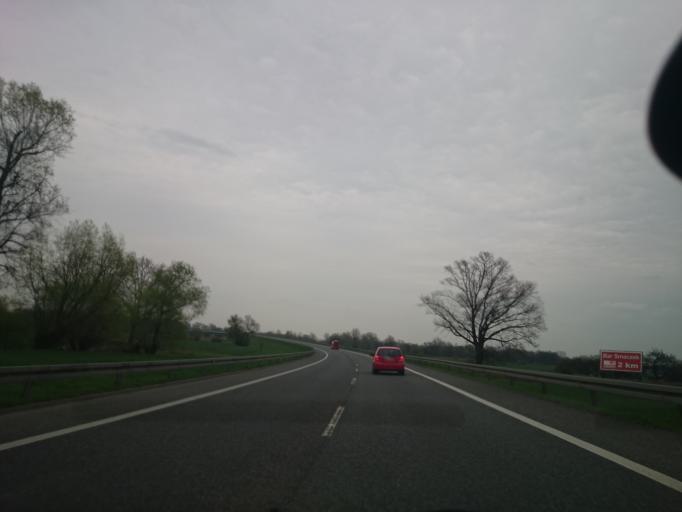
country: PL
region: Opole Voivodeship
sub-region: Powiat nyski
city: Otmuchow
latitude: 50.4561
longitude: 17.1824
